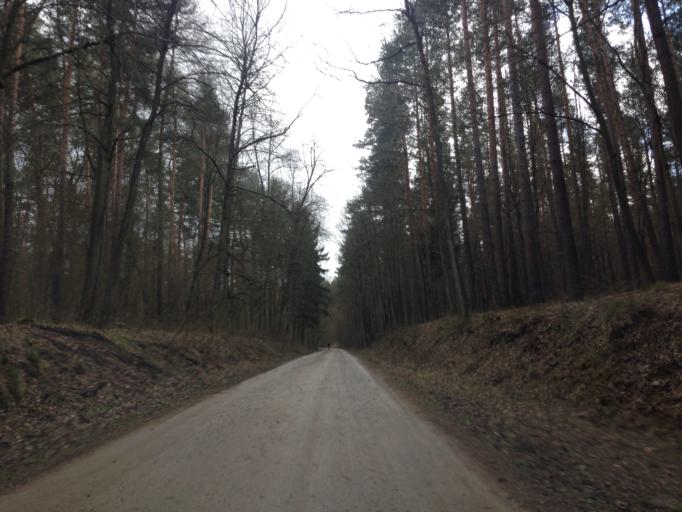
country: PL
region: Kujawsko-Pomorskie
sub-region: Powiat brodnicki
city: Gorzno
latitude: 53.2230
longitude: 19.6690
